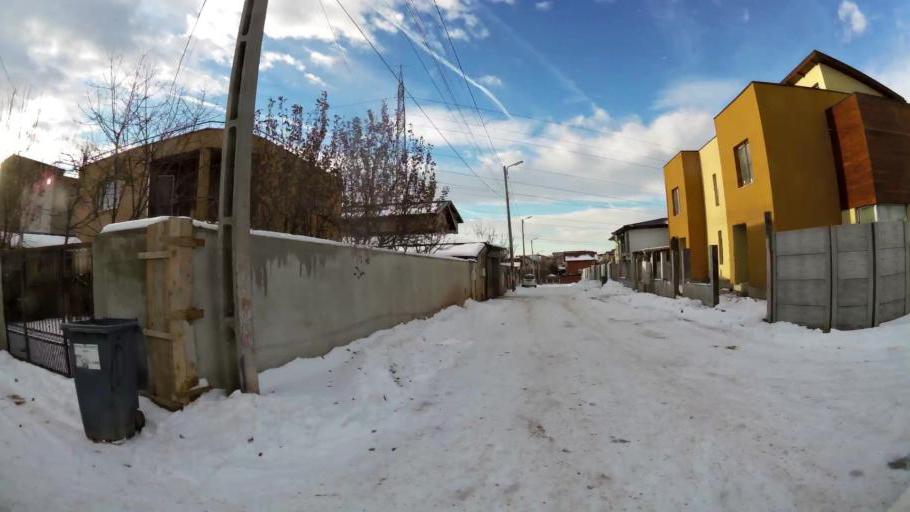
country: RO
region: Ilfov
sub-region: Comuna Fundeni-Dobroesti
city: Fundeni
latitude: 44.4627
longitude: 26.1750
